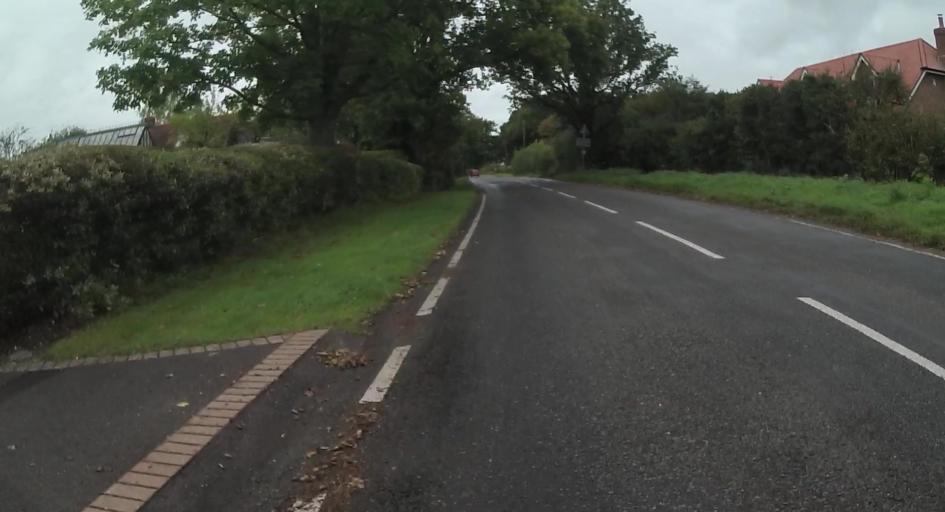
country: GB
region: England
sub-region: Hampshire
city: Tadley
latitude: 51.3447
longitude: -1.1633
